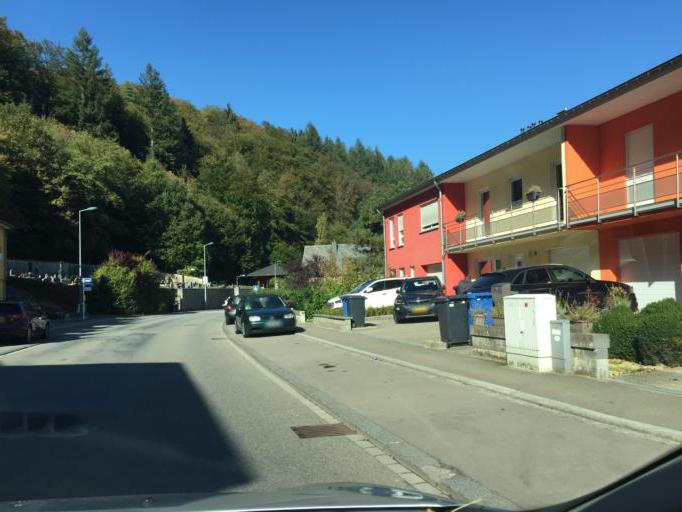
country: LU
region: Luxembourg
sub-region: Canton de Capellen
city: Kopstal
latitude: 49.6685
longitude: 6.0728
